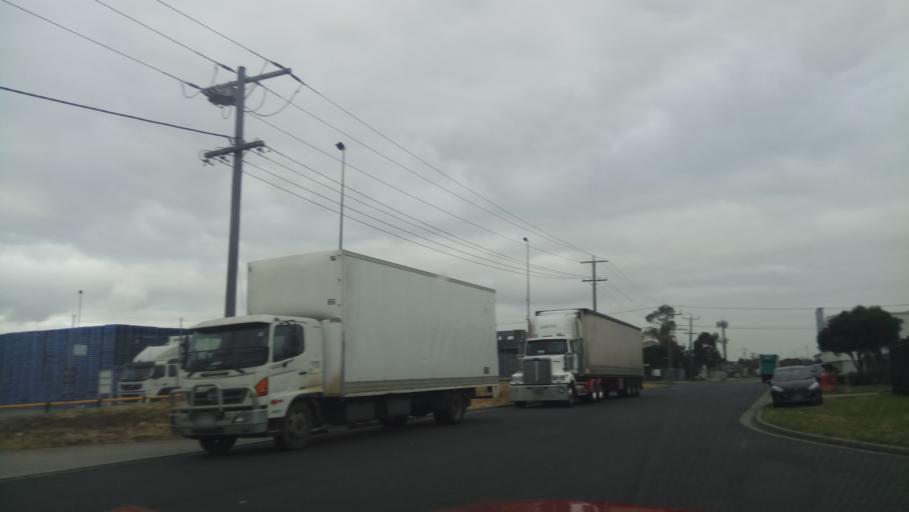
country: AU
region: Victoria
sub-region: Hobsons Bay
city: Altona North
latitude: -37.8405
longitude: 144.8241
